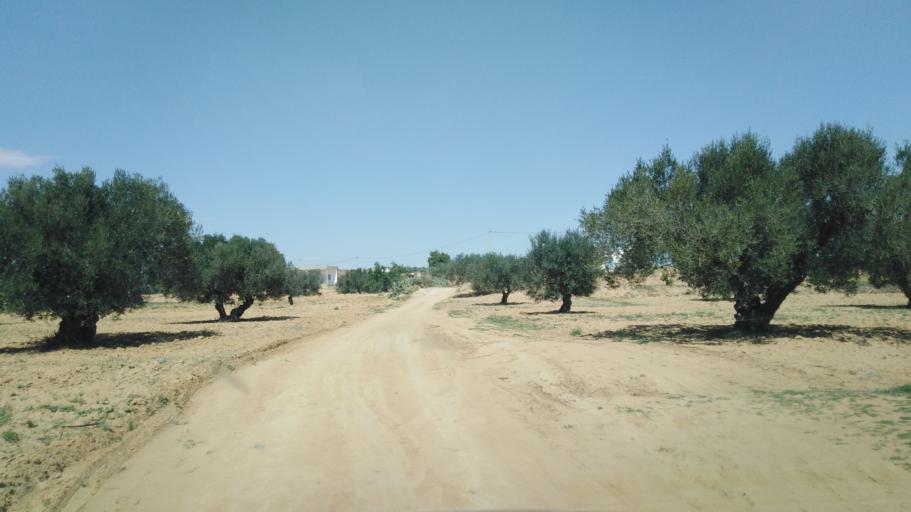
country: TN
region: Safaqis
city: Sfax
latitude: 34.7749
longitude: 10.5275
